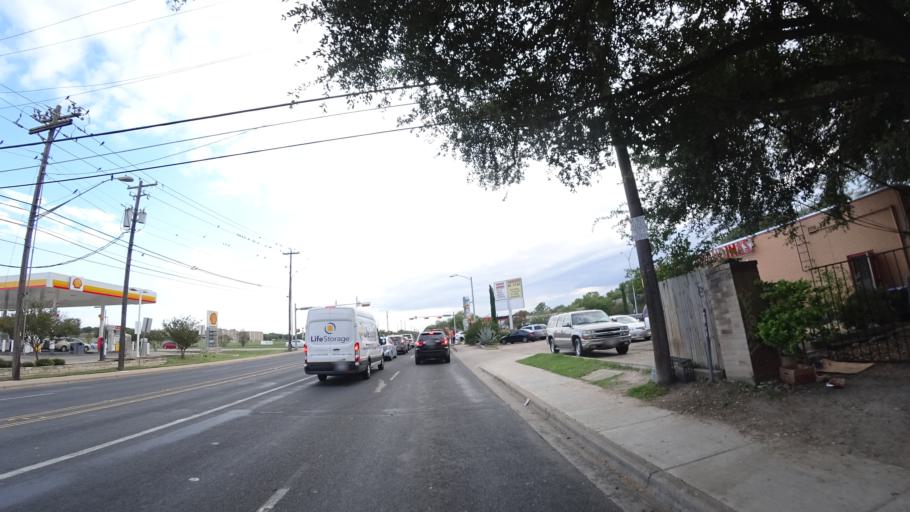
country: US
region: Texas
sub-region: Travis County
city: Onion Creek
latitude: 30.1977
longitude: -97.7875
